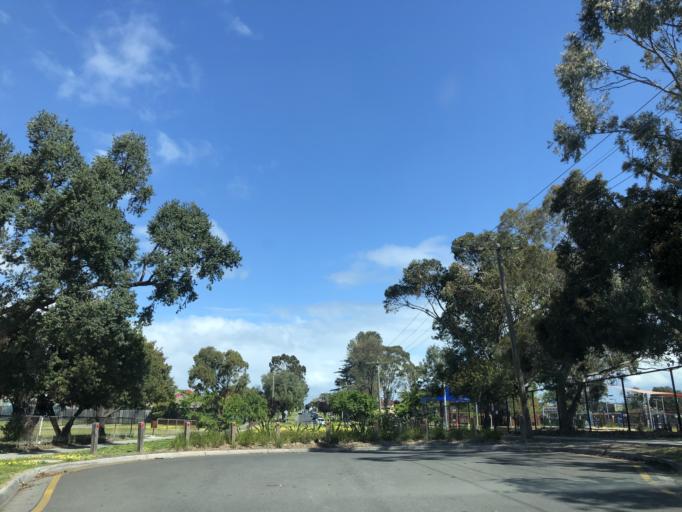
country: AU
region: Victoria
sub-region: Monash
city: Oakleigh South
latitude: -37.9272
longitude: 145.1031
